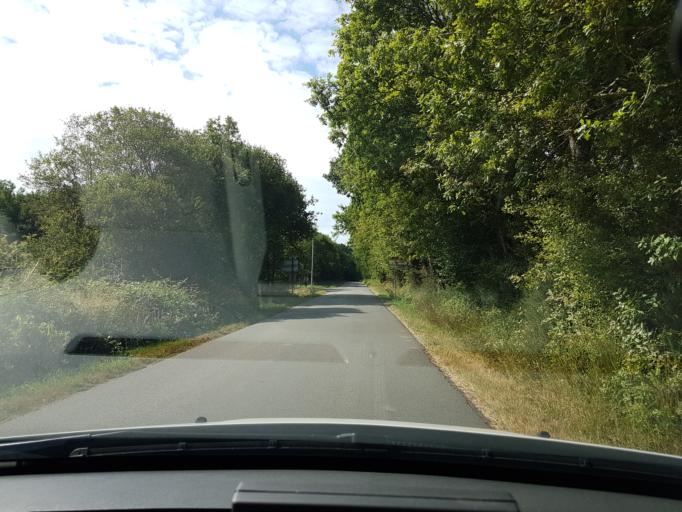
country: FR
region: Brittany
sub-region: Departement du Morbihan
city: Sainte-Helene
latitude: 47.7179
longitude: -3.2096
